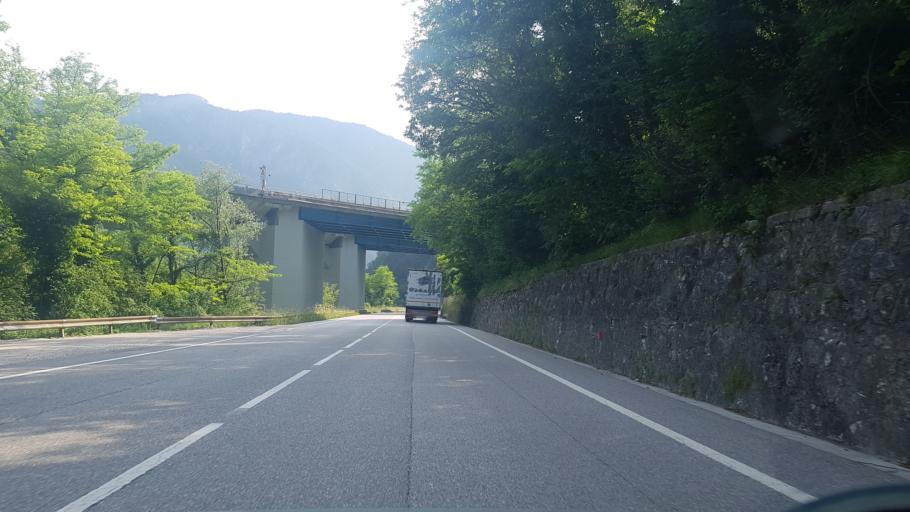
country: IT
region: Friuli Venezia Giulia
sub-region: Provincia di Udine
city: Chiusaforte
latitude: 46.4021
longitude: 13.2880
